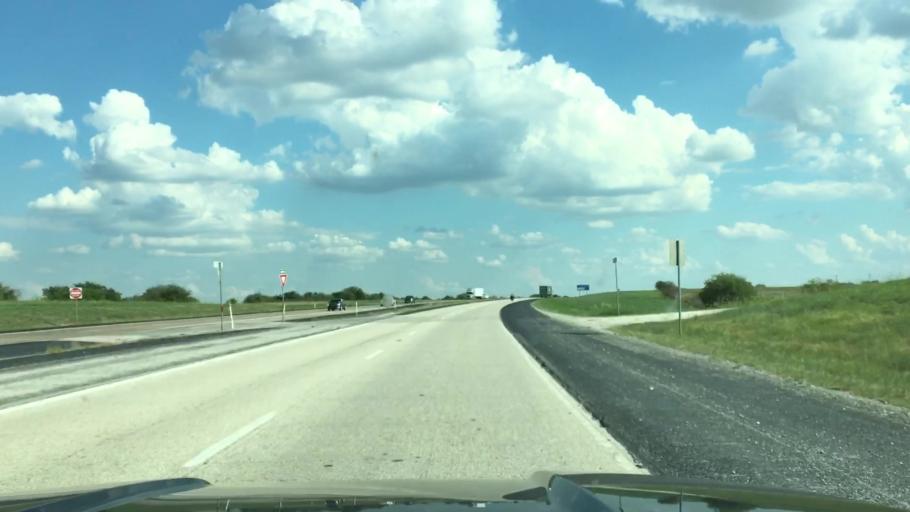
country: US
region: Texas
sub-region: Wise County
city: New Fairview
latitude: 33.1204
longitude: -97.4843
